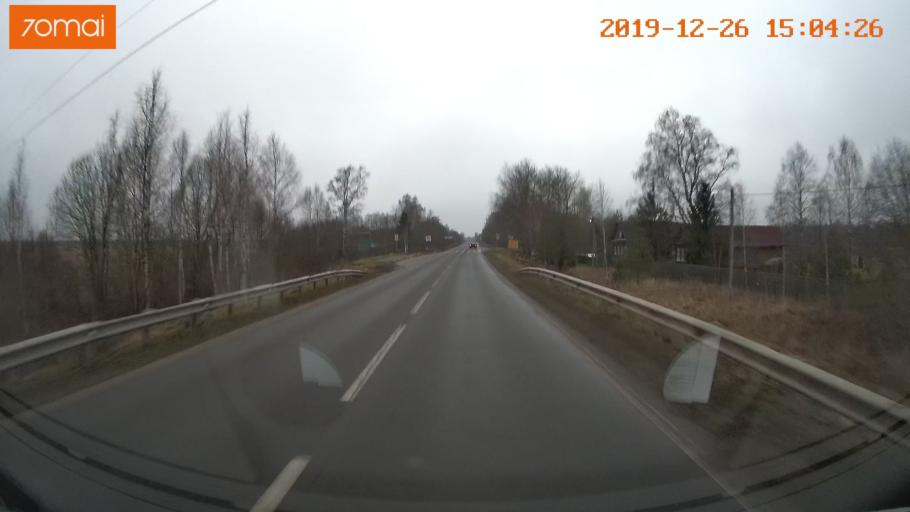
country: RU
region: Jaroslavl
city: Rybinsk
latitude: 58.2000
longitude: 38.8620
